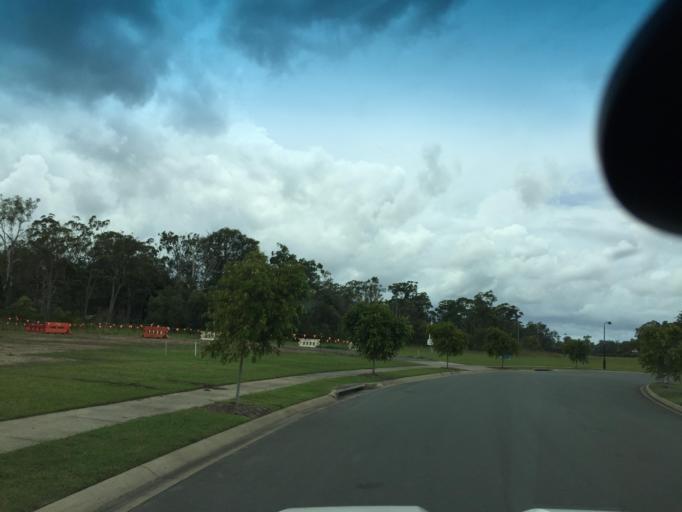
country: AU
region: Queensland
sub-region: Moreton Bay
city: Caboolture
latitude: -27.0607
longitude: 152.9307
